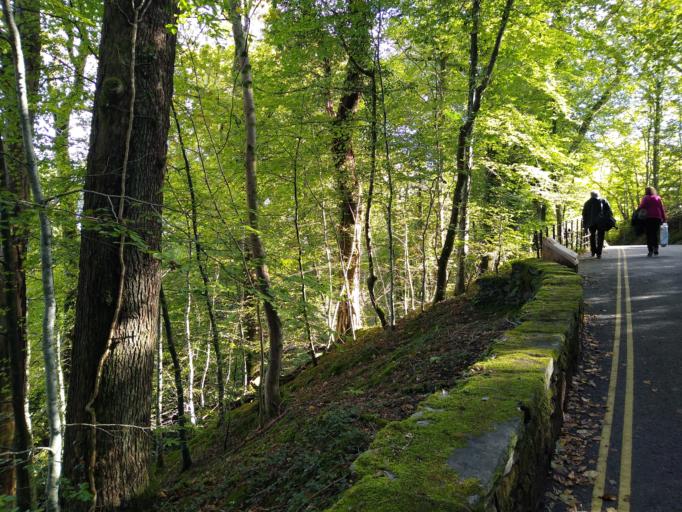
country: GB
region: England
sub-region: Cumbria
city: Ambleside
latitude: 54.4323
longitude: -2.9587
